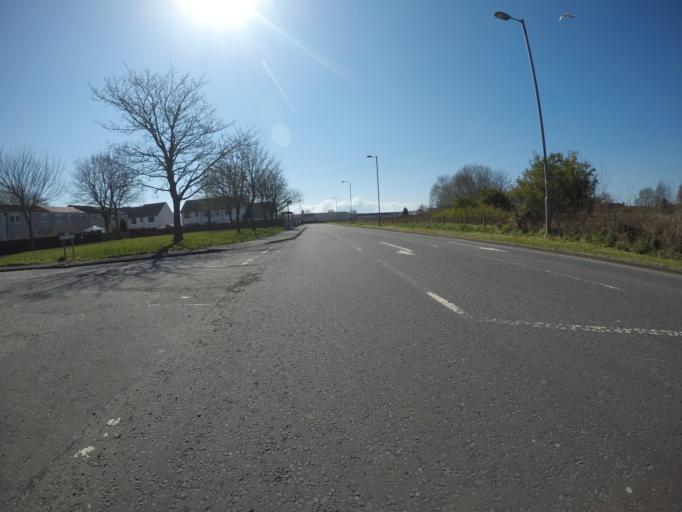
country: GB
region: Scotland
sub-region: North Ayrshire
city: Irvine
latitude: 55.6313
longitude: -4.6677
